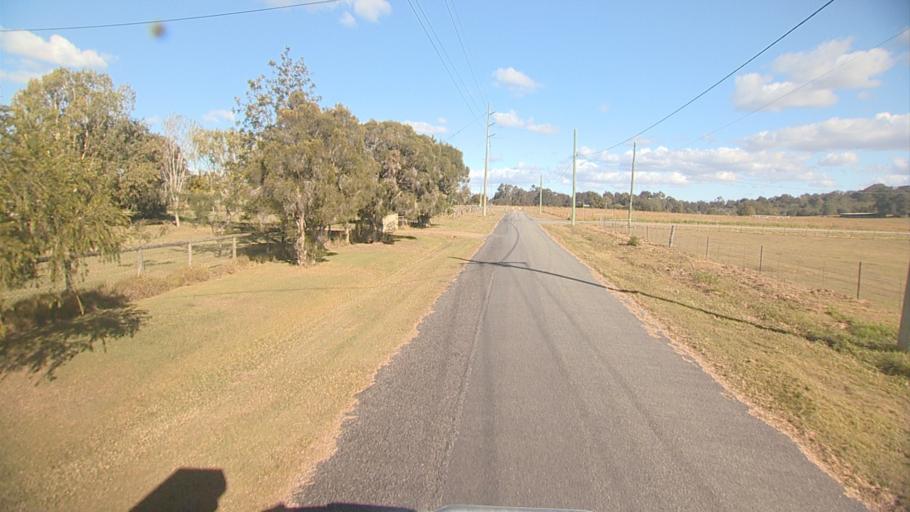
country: AU
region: Queensland
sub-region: Logan
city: Logan Reserve
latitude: -27.7244
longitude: 153.1139
